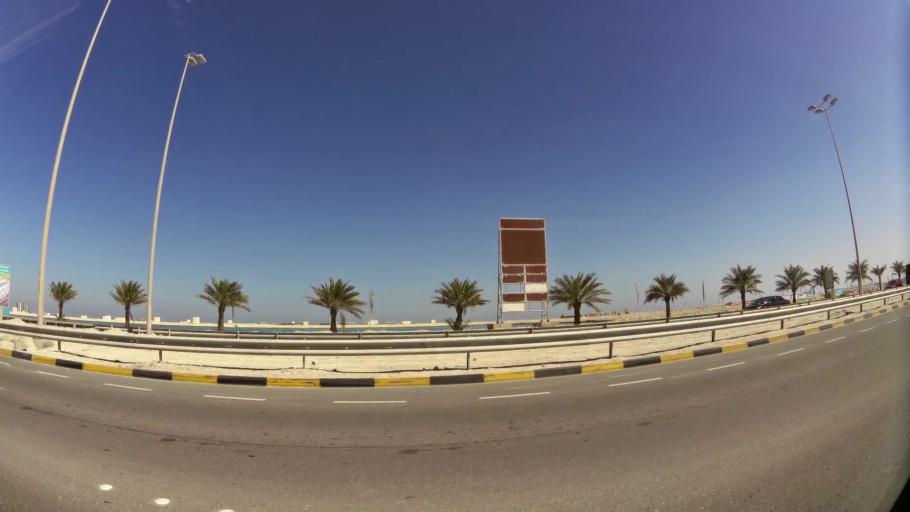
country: BH
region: Muharraq
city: Al Hadd
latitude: 26.2557
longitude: 50.6600
